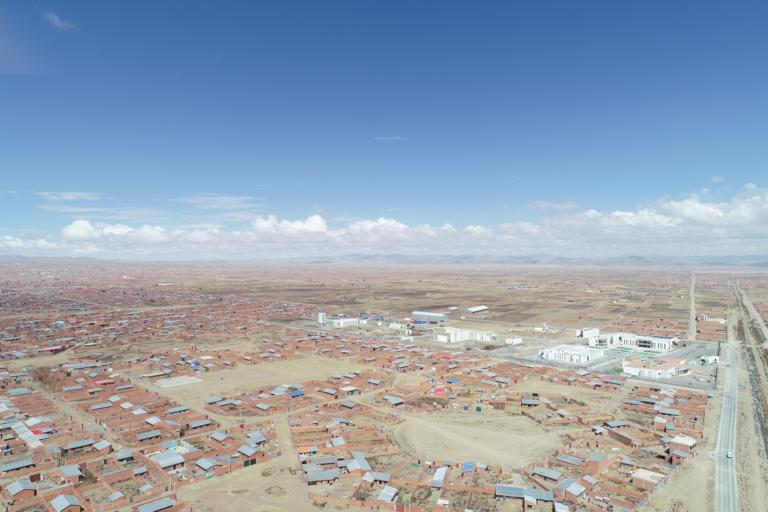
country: BO
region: La Paz
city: La Paz
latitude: -16.5904
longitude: -68.2118
